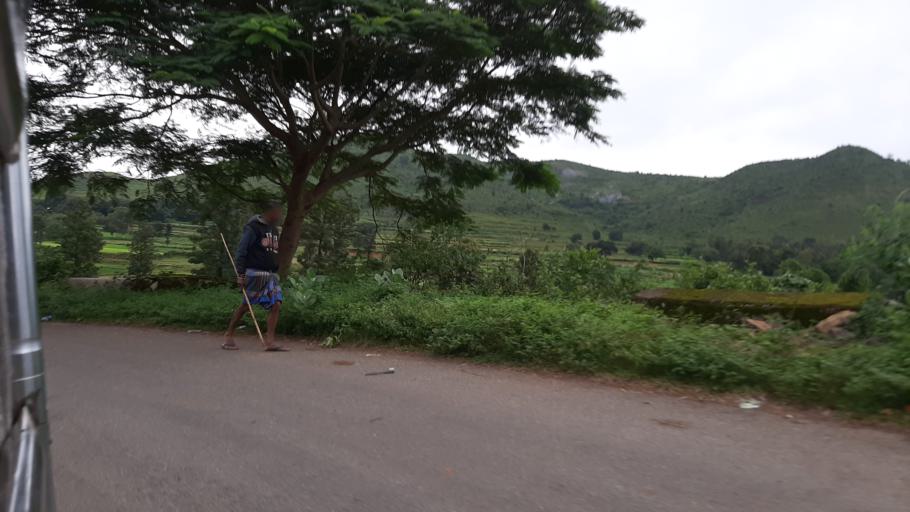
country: IN
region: Andhra Pradesh
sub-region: Vizianagaram District
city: Salur
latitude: 18.2880
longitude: 82.9387
